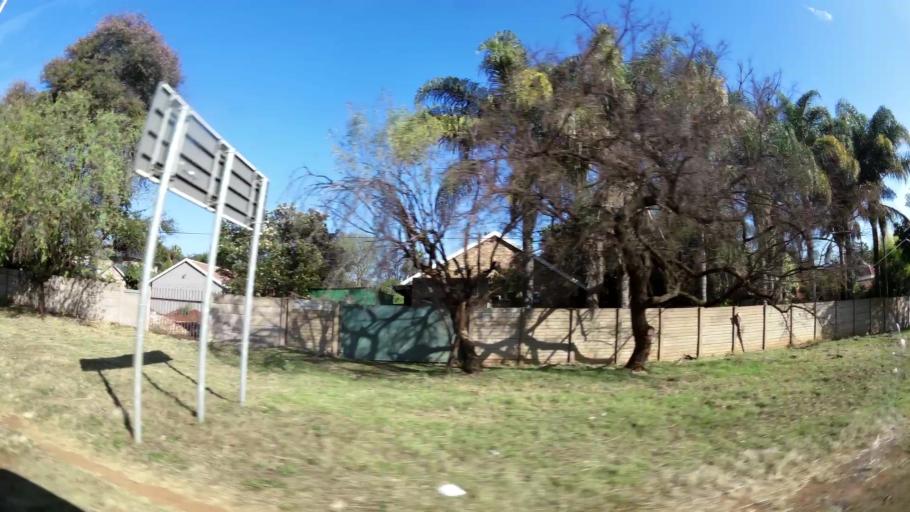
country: ZA
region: Gauteng
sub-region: City of Tshwane Metropolitan Municipality
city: Pretoria
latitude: -25.6509
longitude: 28.2446
